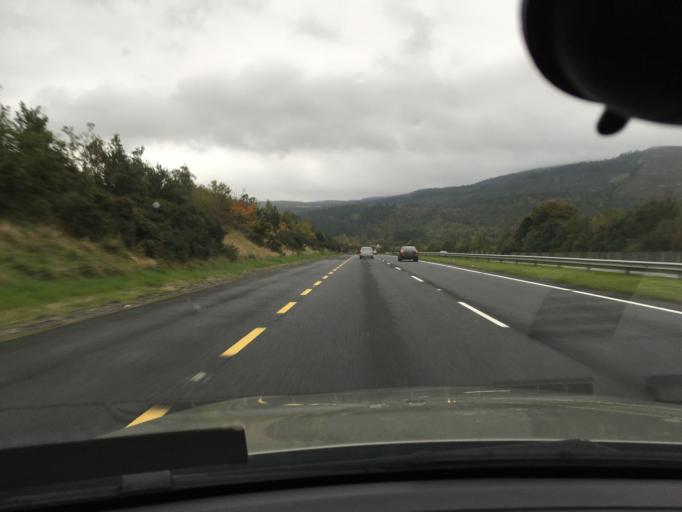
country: IE
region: Leinster
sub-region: Lu
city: Dundalk
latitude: 54.0612
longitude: -6.3554
